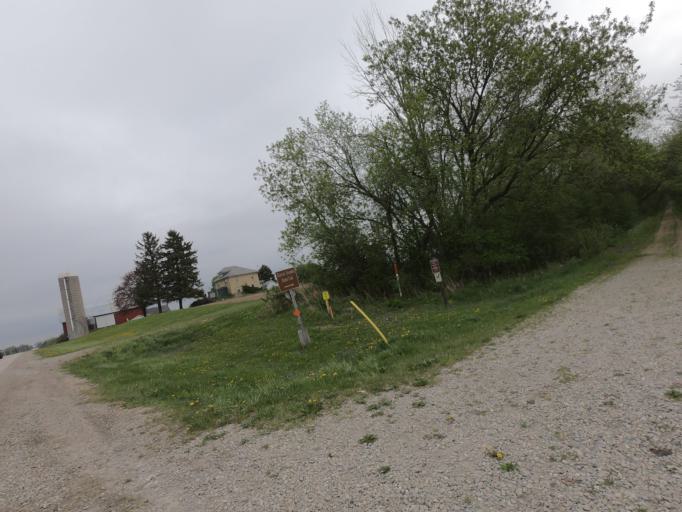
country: US
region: Wisconsin
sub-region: Jefferson County
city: Johnson Creek
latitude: 43.0372
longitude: -88.7733
